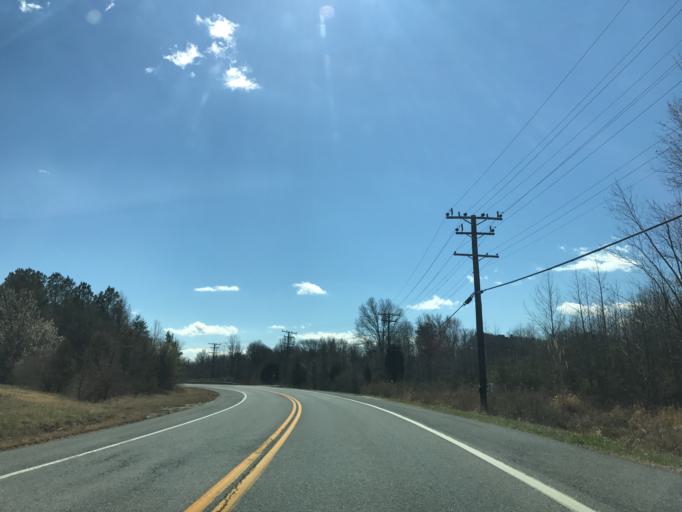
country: US
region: Maryland
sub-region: Anne Arundel County
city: Cape Saint Claire
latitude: 39.0167
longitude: -76.4121
